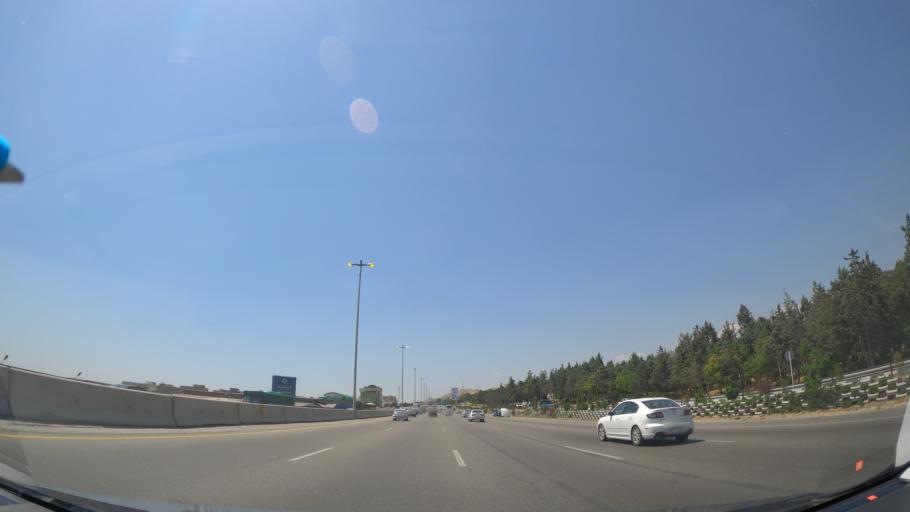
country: IR
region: Alborz
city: Karaj
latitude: 35.7772
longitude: 51.0372
